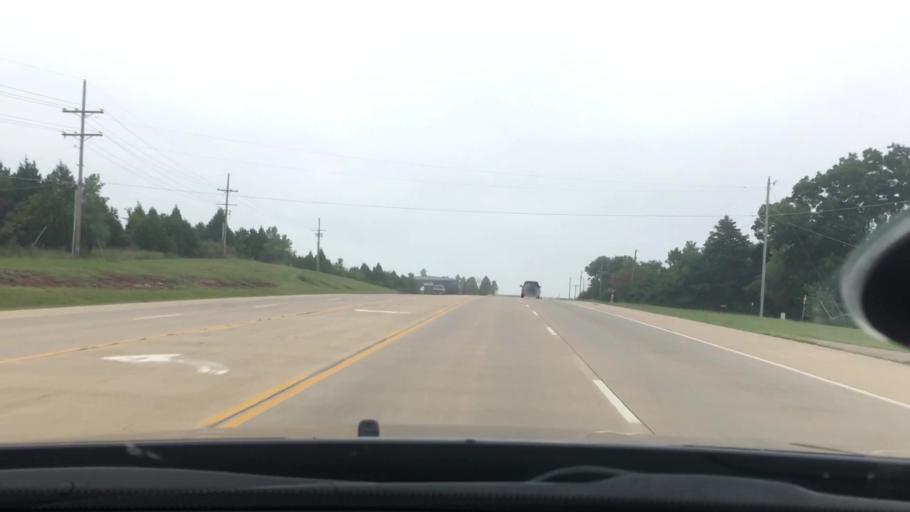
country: US
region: Oklahoma
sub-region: Seminole County
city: Seminole
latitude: 35.2648
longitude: -96.6710
